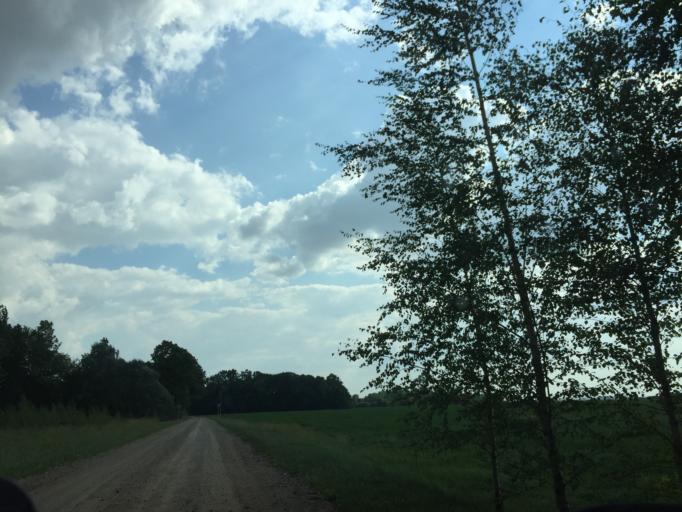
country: LV
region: Jelgava
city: Jelgava
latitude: 56.5099
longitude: 23.7548
